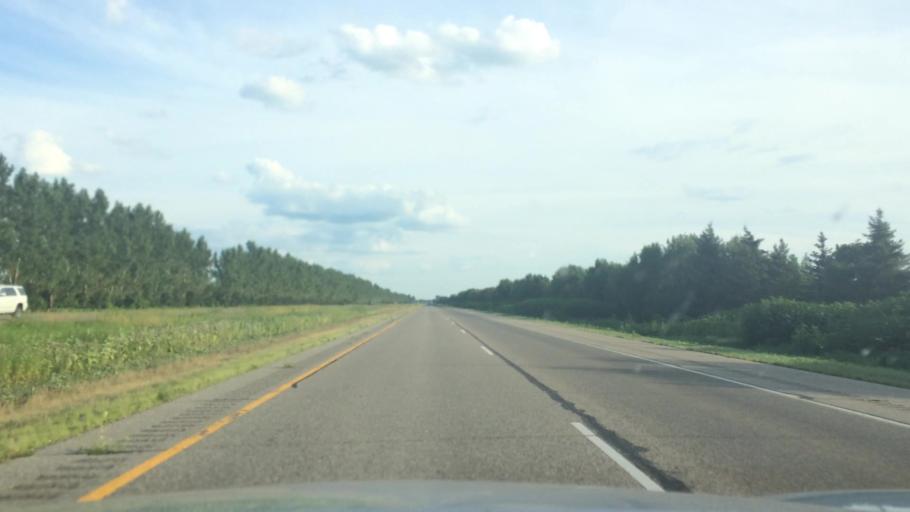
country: US
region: Wisconsin
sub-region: Portage County
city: Plover
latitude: 44.3555
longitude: -89.5213
